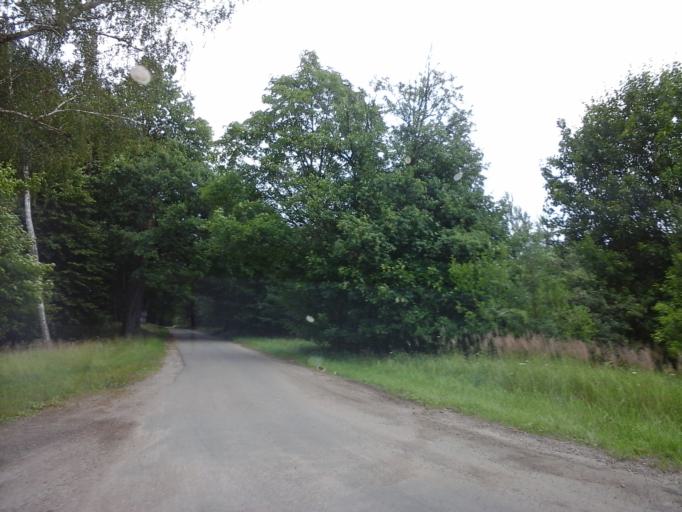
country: PL
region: Lubusz
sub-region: Powiat strzelecko-drezdenecki
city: Dobiegniew
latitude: 53.0922
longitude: 15.7835
